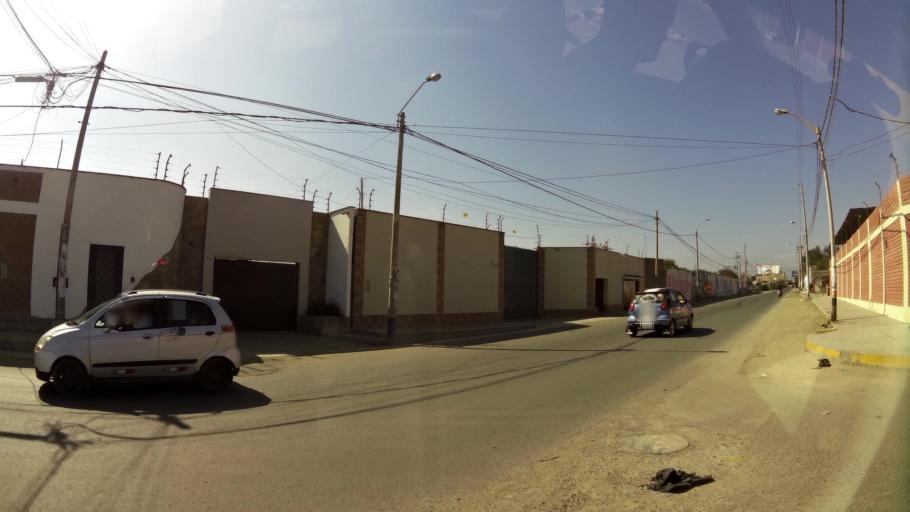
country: PE
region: Ica
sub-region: Provincia de Chincha
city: Sunampe
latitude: -13.4153
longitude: -76.1530
